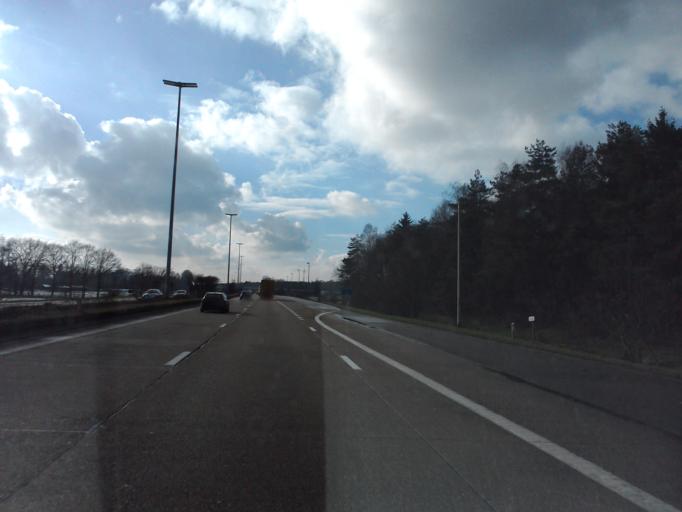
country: BE
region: Flanders
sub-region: Provincie Antwerpen
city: Beerse
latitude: 51.2896
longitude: 4.8638
